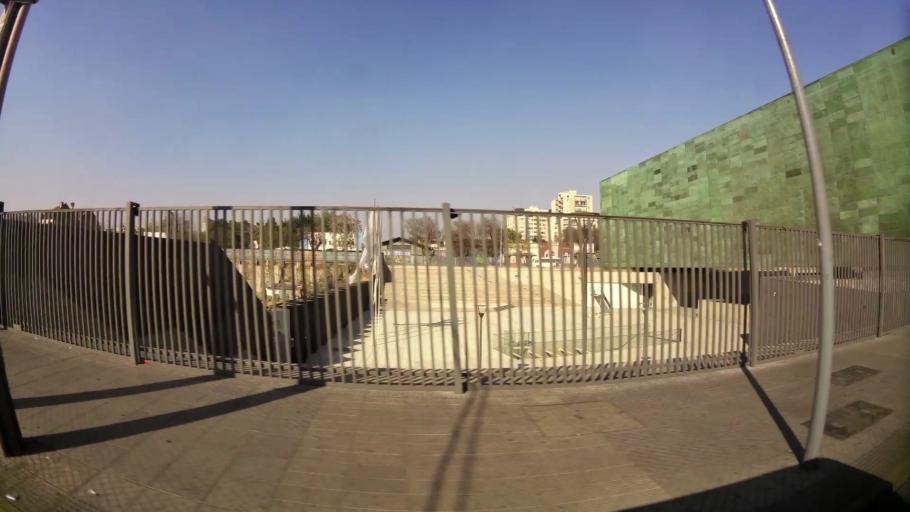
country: CL
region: Santiago Metropolitan
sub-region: Provincia de Santiago
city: Santiago
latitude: -33.4394
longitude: -70.6799
